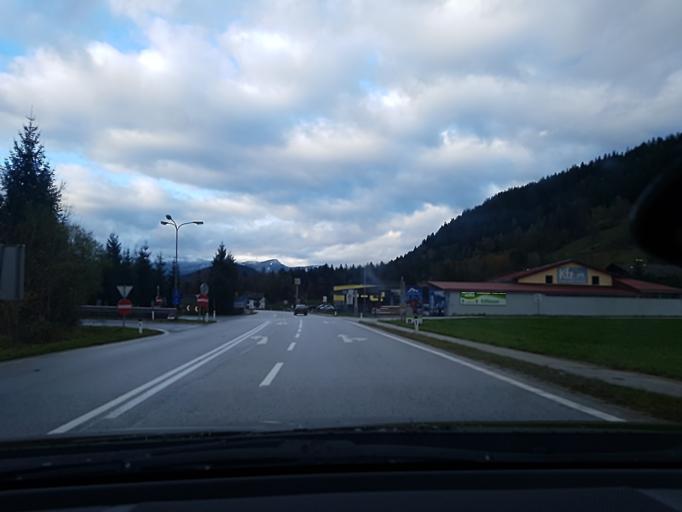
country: AT
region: Styria
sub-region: Politischer Bezirk Liezen
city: Ardning
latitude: 47.6489
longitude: 14.3368
